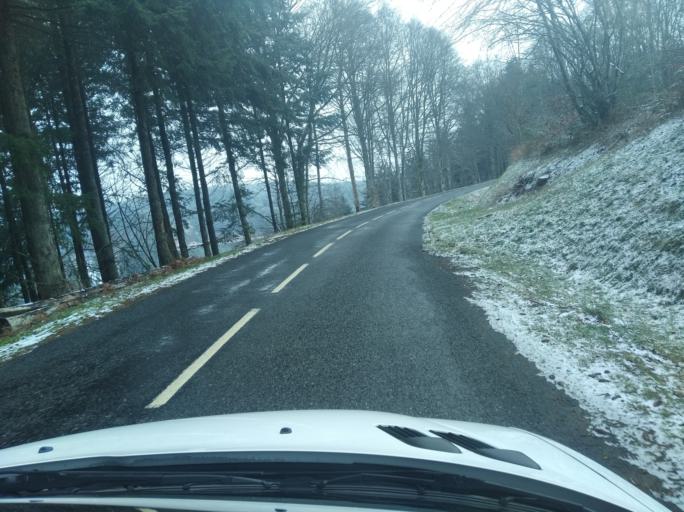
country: FR
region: Rhone-Alpes
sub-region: Departement de la Loire
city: La Pacaudiere
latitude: 46.1240
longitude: 3.7872
